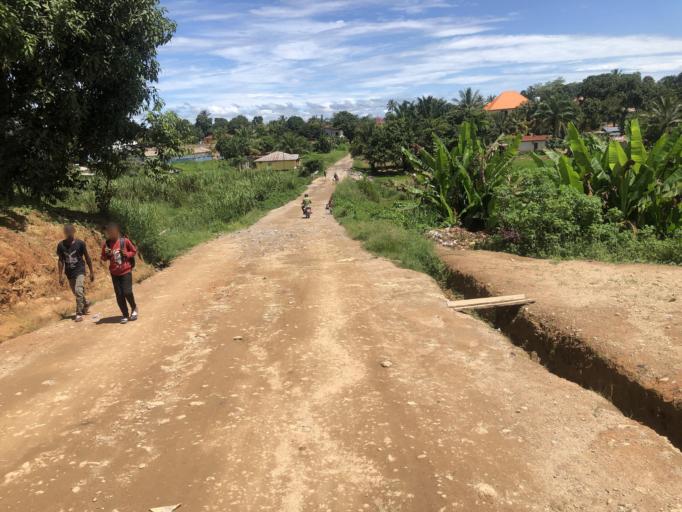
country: SL
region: Eastern Province
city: Koidu
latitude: 8.6437
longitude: -10.9579
